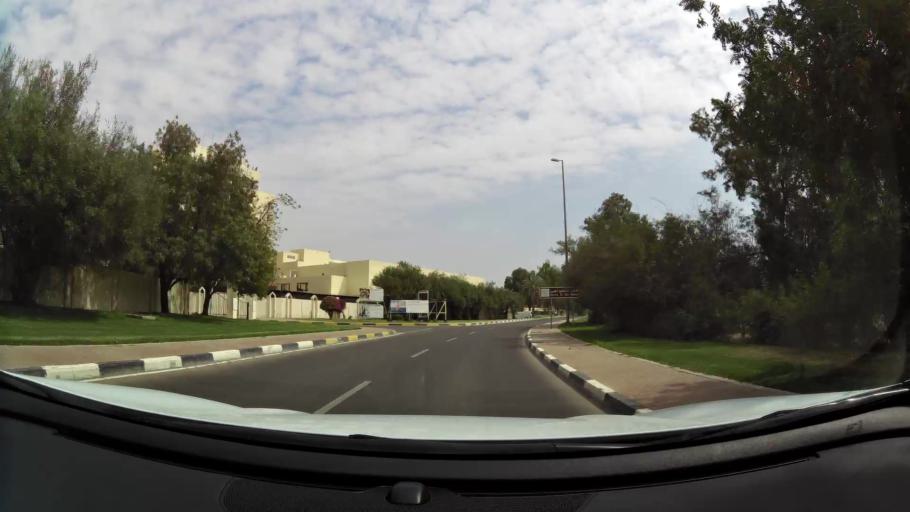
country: OM
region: Al Buraimi
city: Al Buraymi
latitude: 24.2077
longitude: 55.8036
